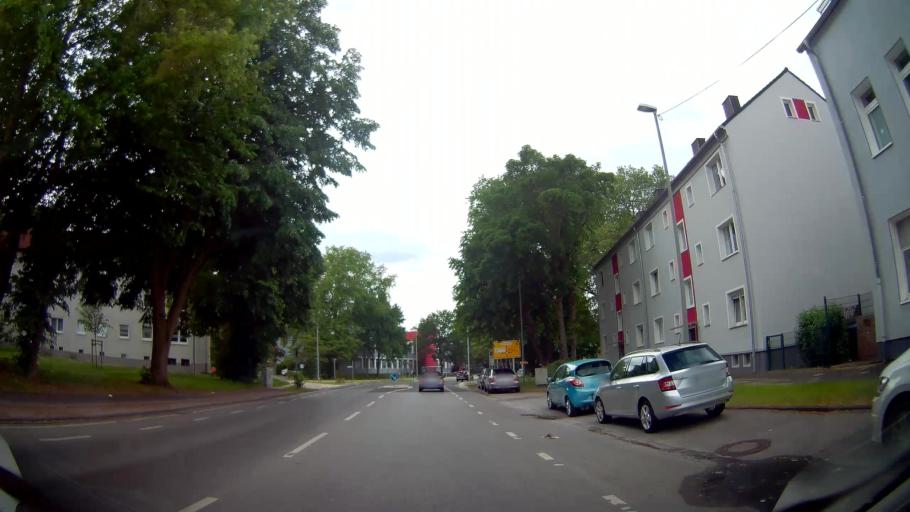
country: DE
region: North Rhine-Westphalia
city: Bochum-Hordel
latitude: 51.5226
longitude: 7.1823
